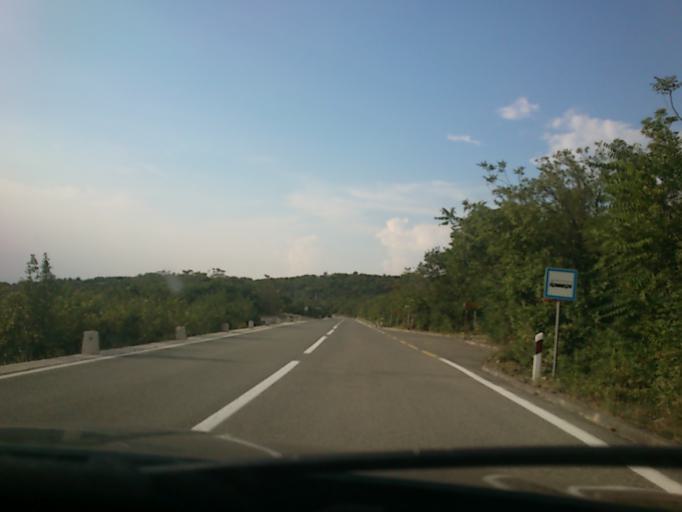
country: HR
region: Primorsko-Goranska
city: Banjol
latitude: 44.7585
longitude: 14.9038
